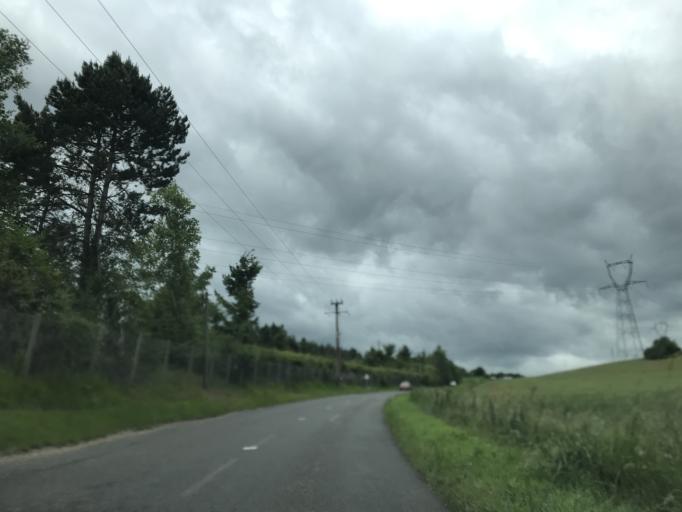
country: FR
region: Haute-Normandie
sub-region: Departement de l'Eure
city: Garennes-sur-Eure
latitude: 48.8995
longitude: 1.4286
